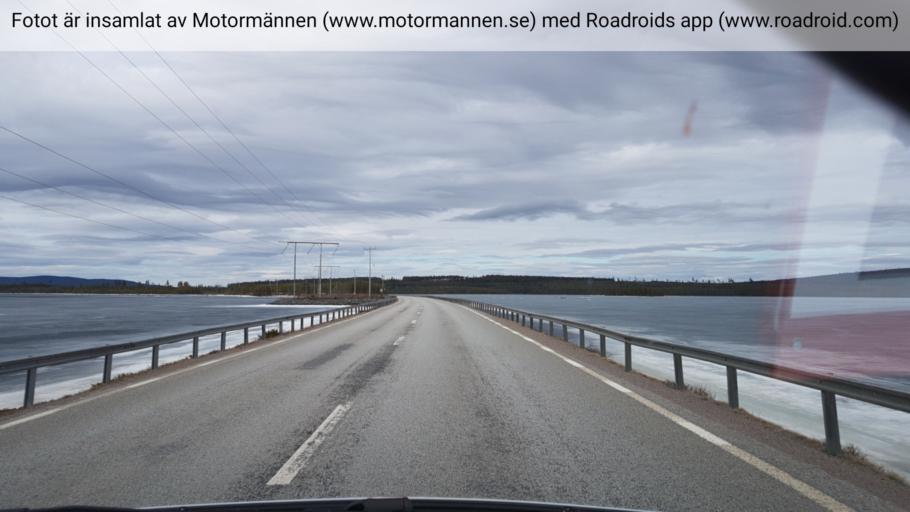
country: SE
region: Vaesterbotten
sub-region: Asele Kommun
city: Asele
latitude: 63.8870
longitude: 17.2120
